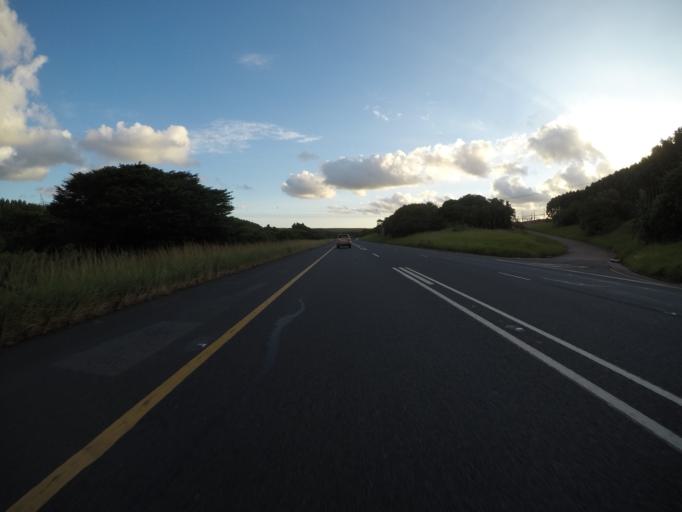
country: ZA
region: KwaZulu-Natal
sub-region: uThungulu District Municipality
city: Richards Bay
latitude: -28.6862
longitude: 32.0395
